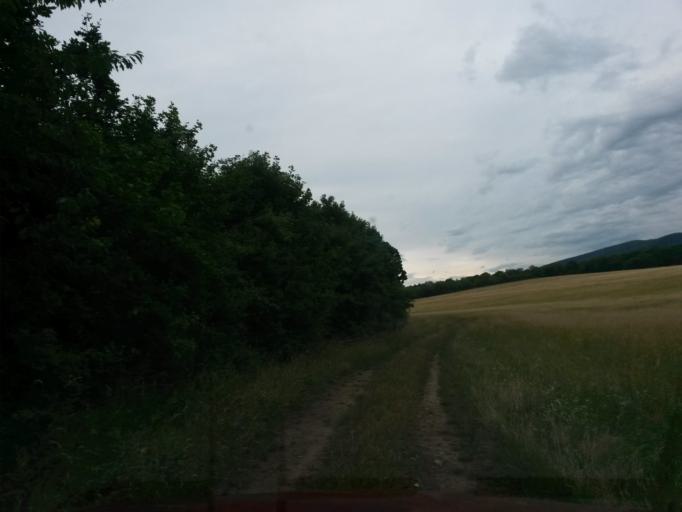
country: SK
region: Banskobystricky
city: Velky Krtis
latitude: 48.3161
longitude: 19.4197
